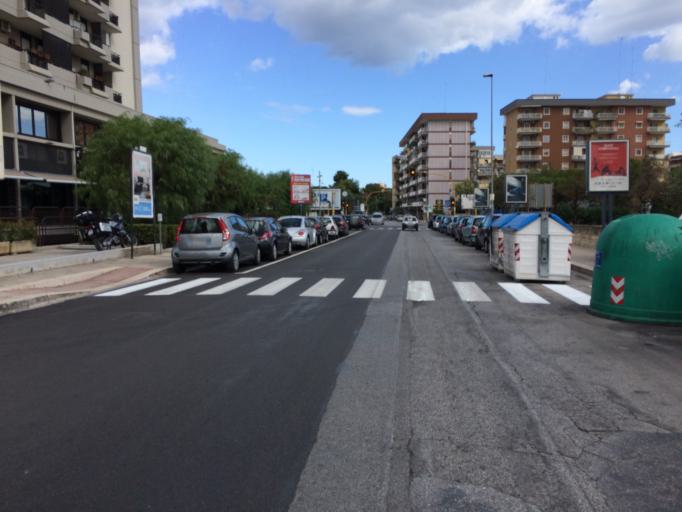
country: IT
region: Apulia
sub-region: Provincia di Bari
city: Bari
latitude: 41.0985
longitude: 16.8558
